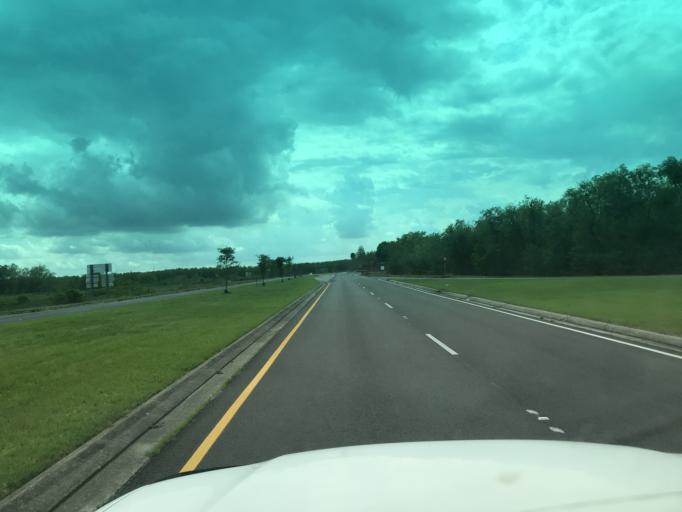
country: US
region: Louisiana
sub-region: Saint Bernard Parish
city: Chalmette
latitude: 30.0426
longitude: -89.9403
